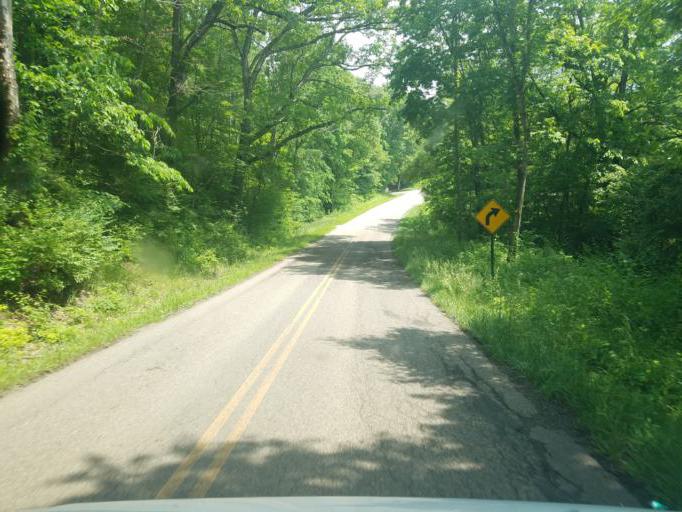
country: US
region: Ohio
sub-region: Knox County
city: Oak Hill
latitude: 40.3843
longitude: -82.2677
